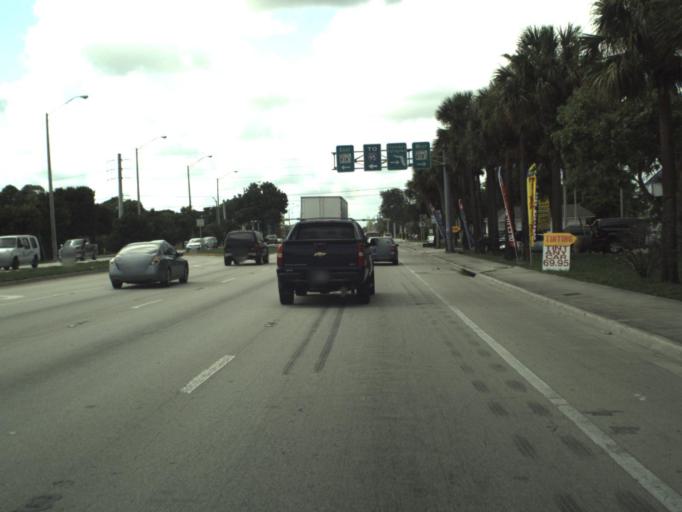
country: US
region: Florida
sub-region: Broward County
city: Davie
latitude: 26.0654
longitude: -80.2081
